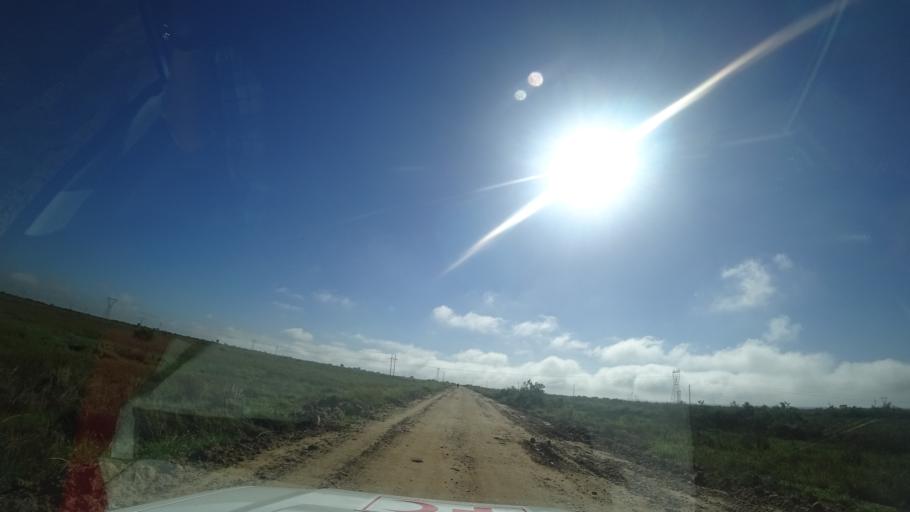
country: MZ
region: Sofala
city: Dondo
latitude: -19.4653
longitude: 34.5603
